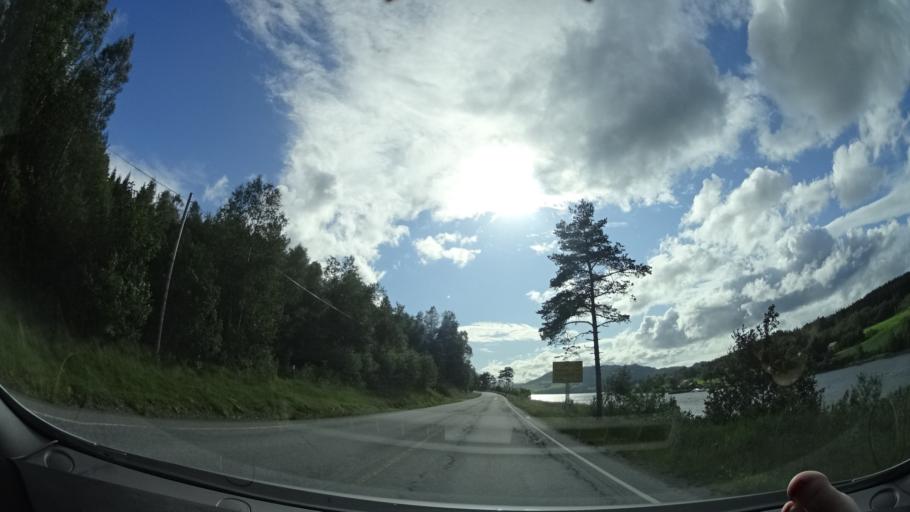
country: NO
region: More og Romsdal
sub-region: Halsa
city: Liaboen
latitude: 63.0856
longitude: 8.3491
